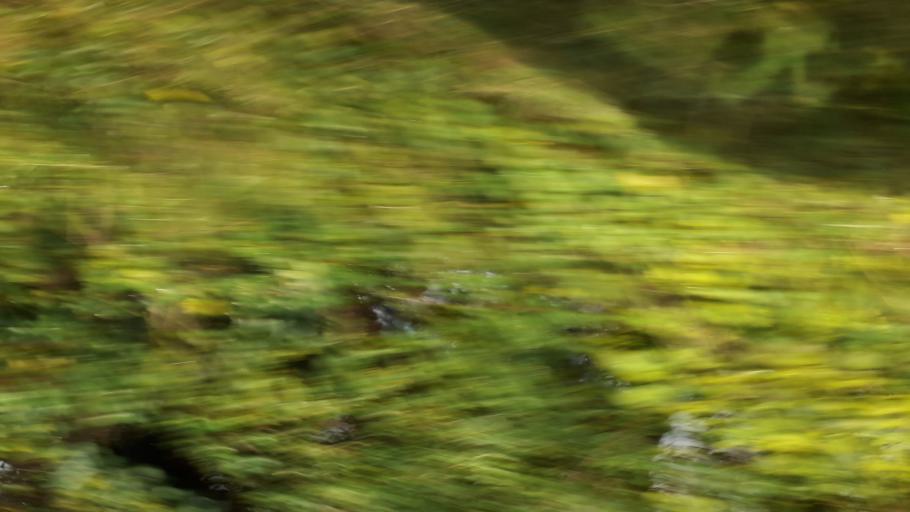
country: IE
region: Leinster
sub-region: An Longfort
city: Lanesborough
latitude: 53.7693
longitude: -8.1028
